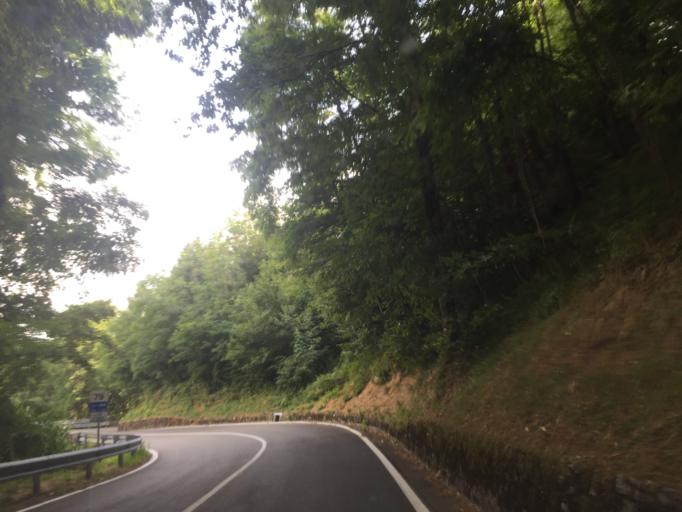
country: IT
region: Tuscany
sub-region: Provincia di Pistoia
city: Cutigliano
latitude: 44.1115
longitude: 10.7356
